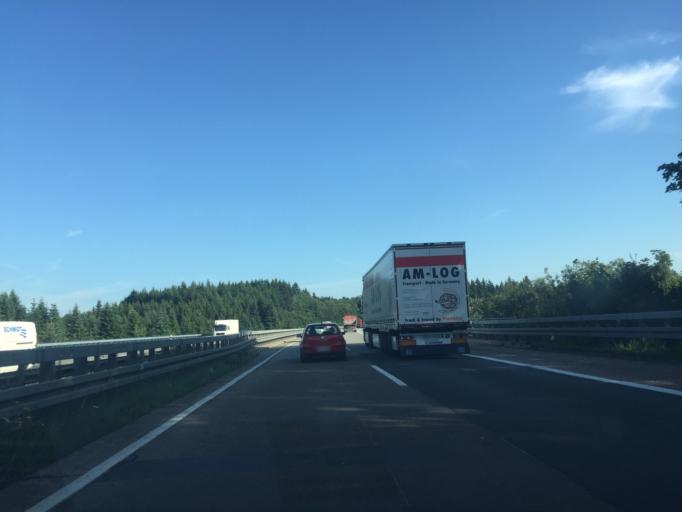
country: DE
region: North Rhine-Westphalia
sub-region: Regierungsbezirk Arnsberg
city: Luedenscheid
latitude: 51.1702
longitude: 7.6533
